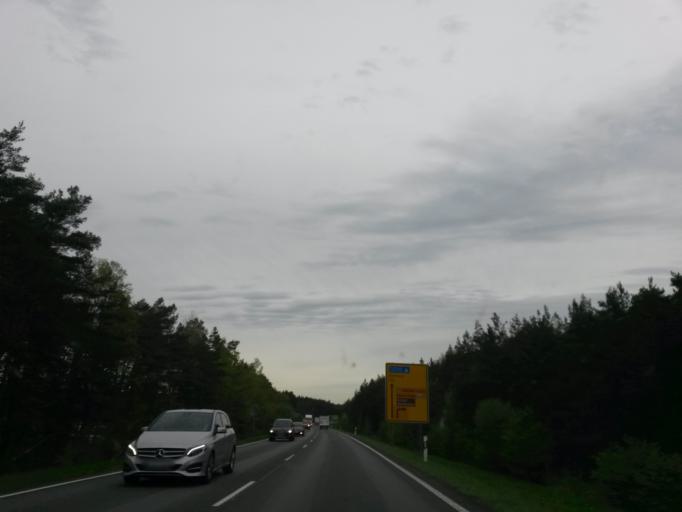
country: DE
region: Bavaria
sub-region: Upper Franconia
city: Pommersfelden
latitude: 49.7358
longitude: 10.8269
